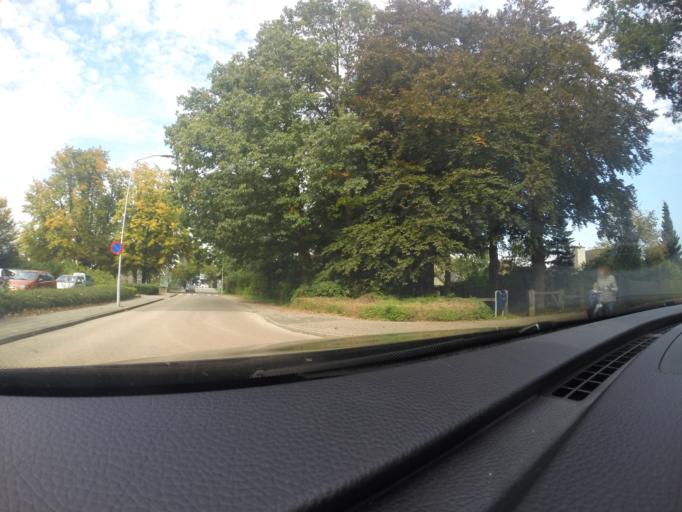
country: NL
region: Gelderland
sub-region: Gemeente Doetinchem
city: Doetinchem
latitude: 51.9642
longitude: 6.2127
